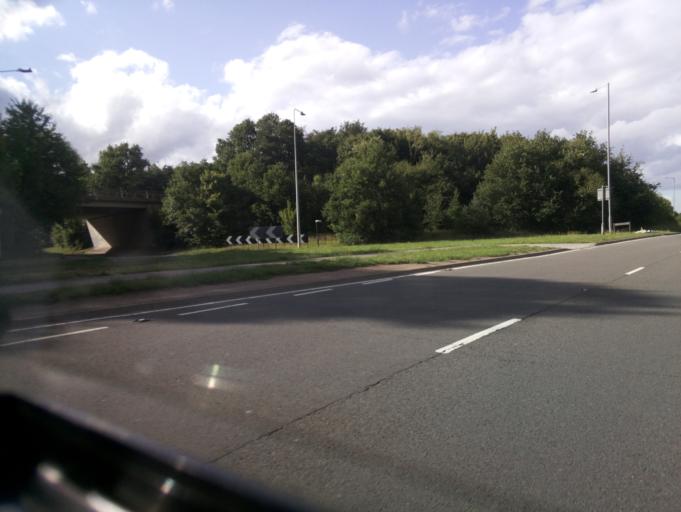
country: GB
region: England
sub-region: Warwickshire
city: Warwick
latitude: 52.3071
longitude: -1.5729
